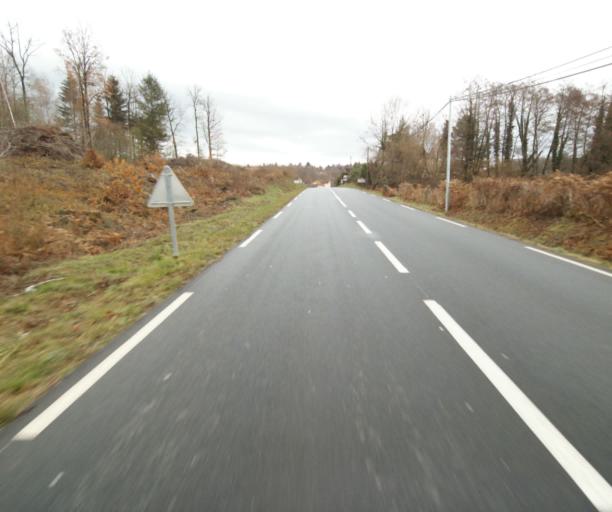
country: FR
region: Limousin
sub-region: Departement de la Correze
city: Saint-Mexant
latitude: 45.2763
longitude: 1.6291
